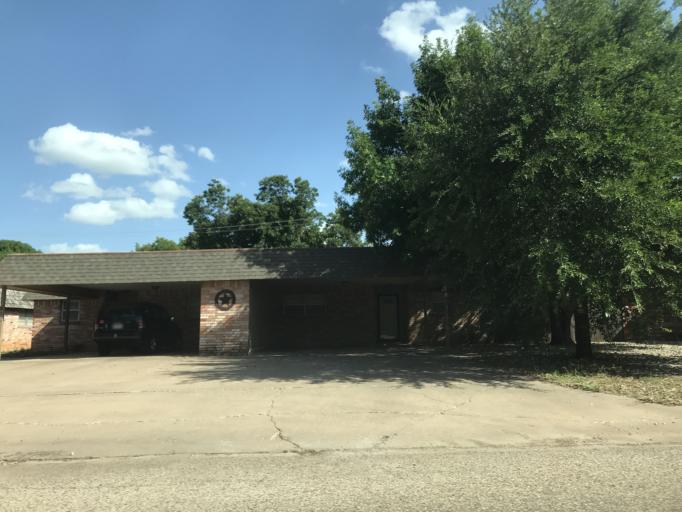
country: US
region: Texas
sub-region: Taylor County
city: Abilene
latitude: 32.4305
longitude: -99.7643
